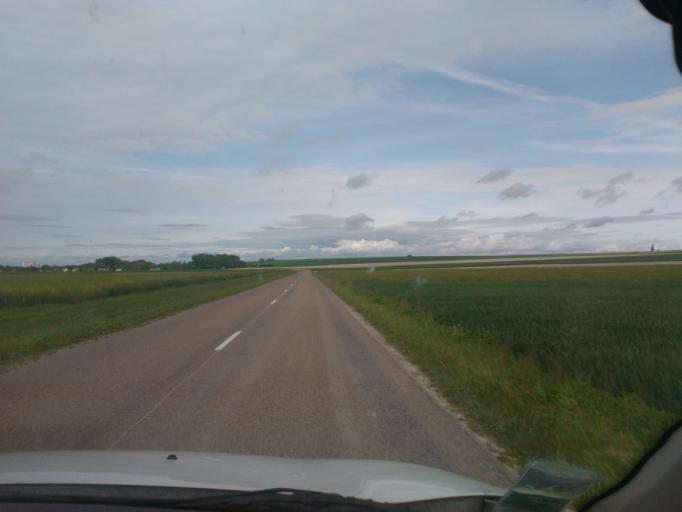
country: FR
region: Champagne-Ardenne
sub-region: Departement de l'Aube
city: Marigny-le-Chatel
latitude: 48.3620
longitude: 3.7281
